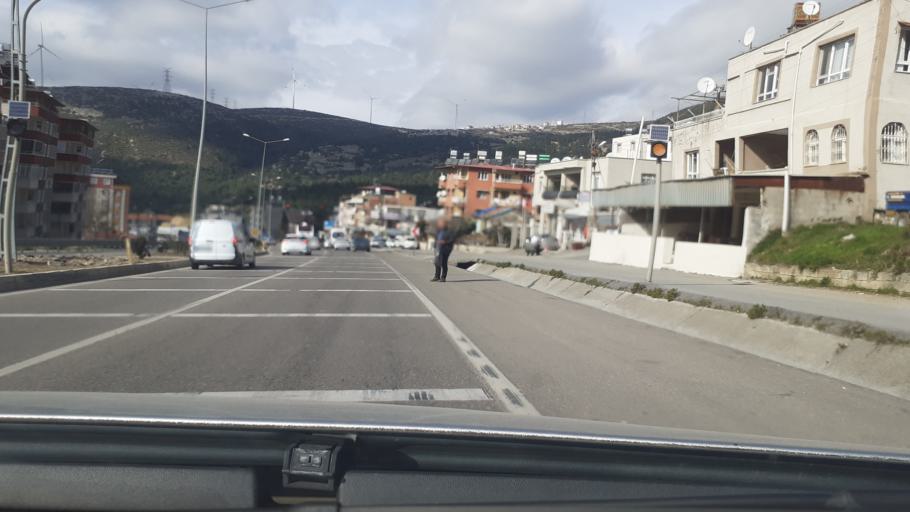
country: TR
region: Hatay
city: Belen
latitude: 36.4867
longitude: 36.2240
